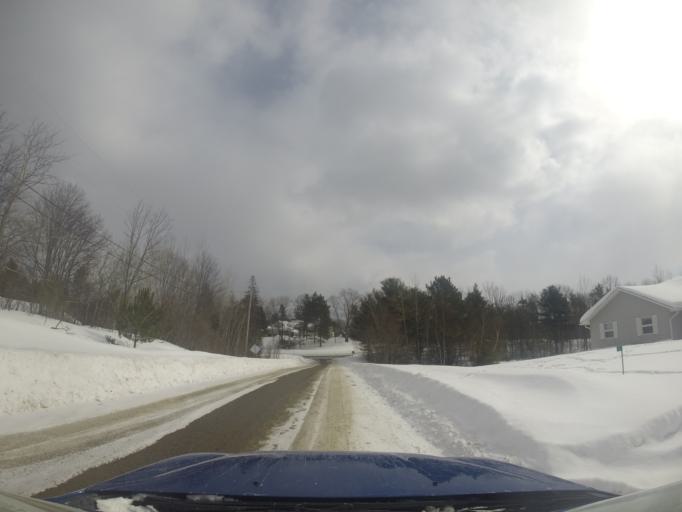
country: CA
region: Ontario
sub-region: Parry Sound District
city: Parry Sound
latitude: 45.3904
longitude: -80.0291
